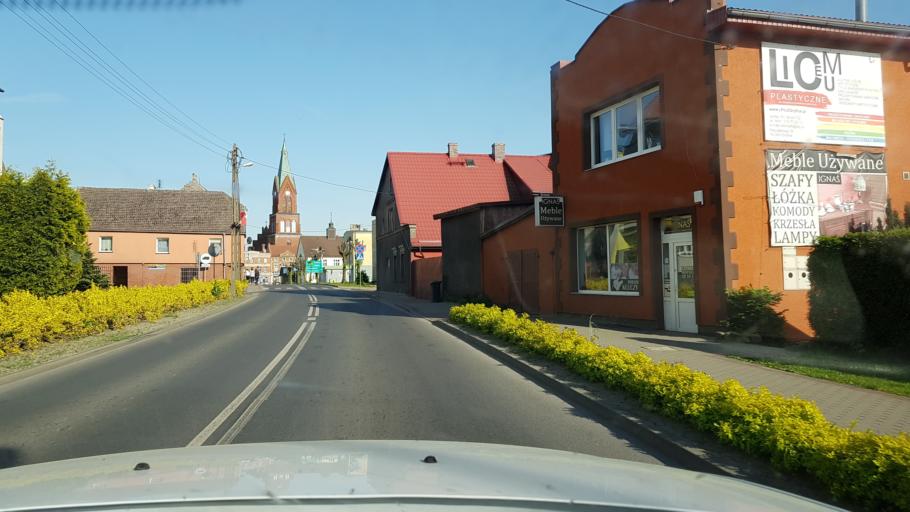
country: PL
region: West Pomeranian Voivodeship
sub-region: Powiat lobeski
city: Resko
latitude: 53.7736
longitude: 15.4025
